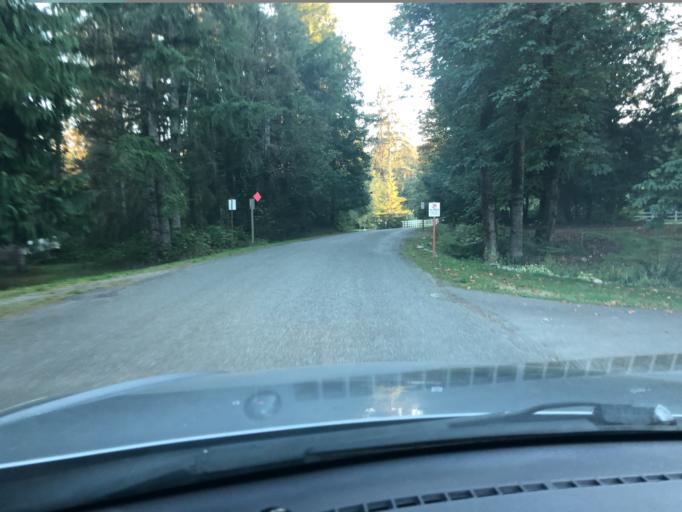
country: US
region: Washington
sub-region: King County
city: Snoqualmie
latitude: 47.5531
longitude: -121.8438
